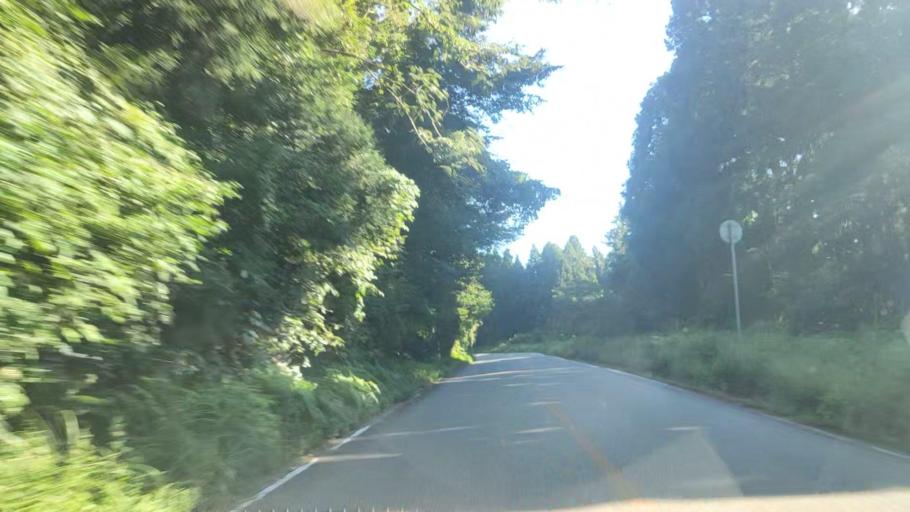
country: JP
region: Ishikawa
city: Nanao
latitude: 37.1055
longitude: 136.9473
